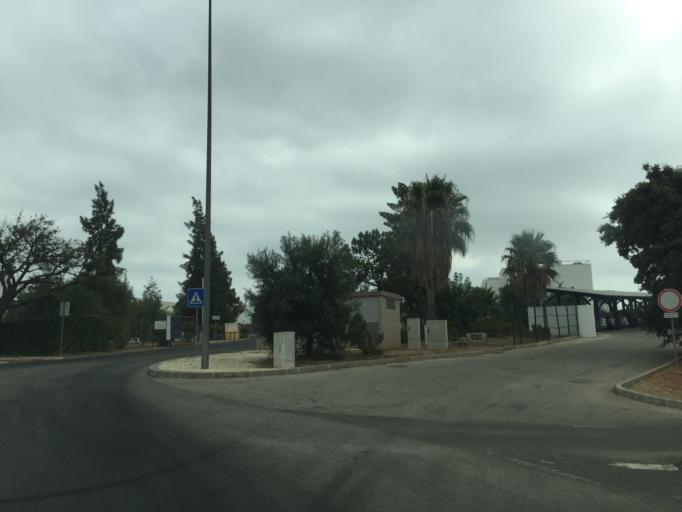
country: PT
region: Faro
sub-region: Faro
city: Santa Barbara de Nexe
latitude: 37.0779
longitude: -7.9757
